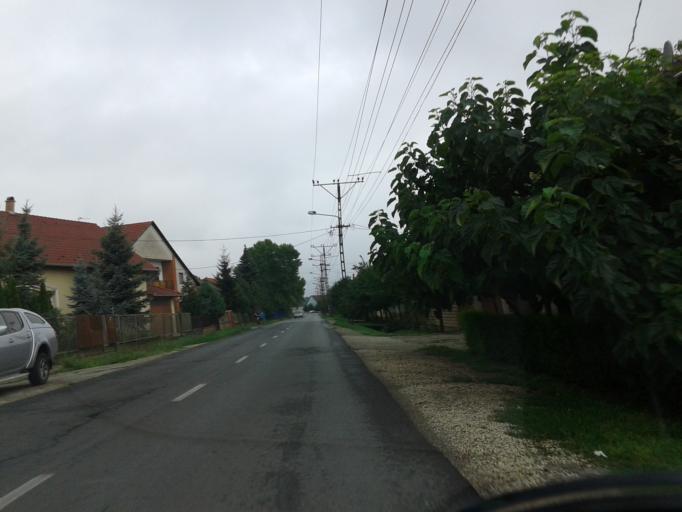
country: HU
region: Csongrad
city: Szeged
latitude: 46.2586
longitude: 20.1864
